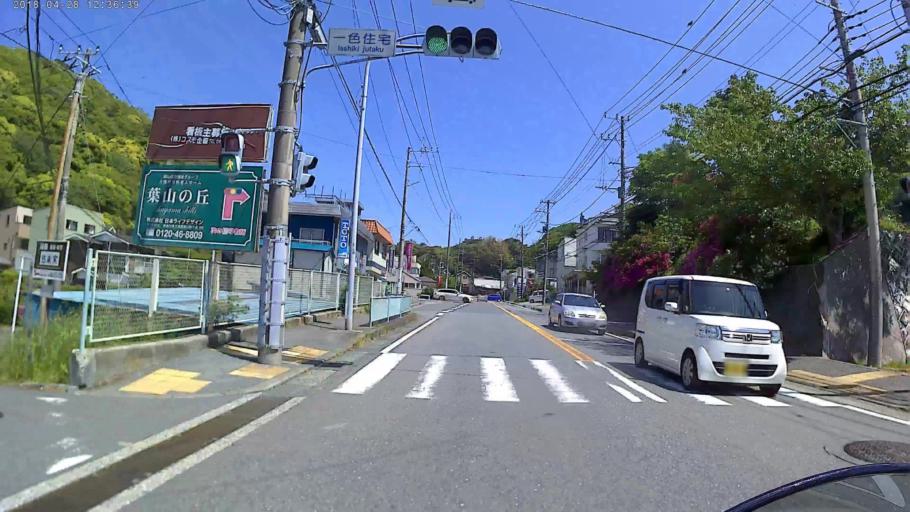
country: JP
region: Kanagawa
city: Hayama
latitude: 35.2652
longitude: 139.5937
